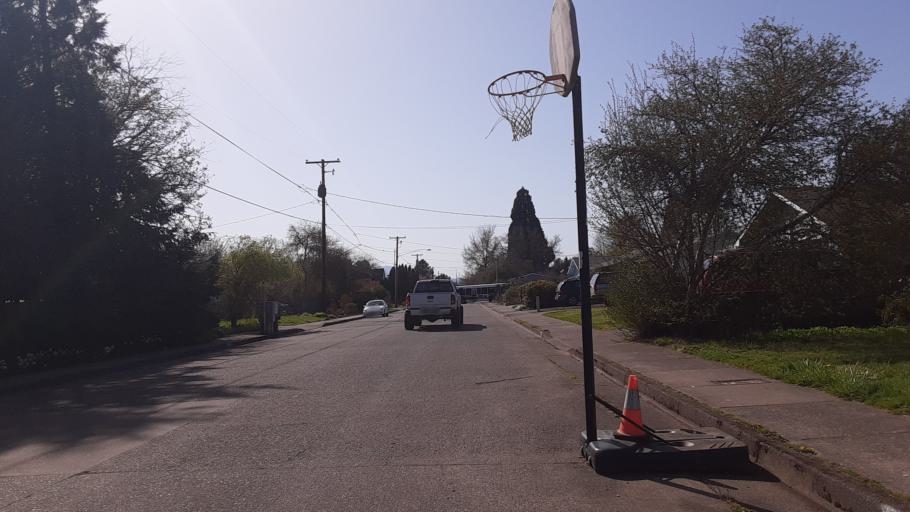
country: US
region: Oregon
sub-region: Benton County
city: Corvallis
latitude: 44.5387
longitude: -123.2590
